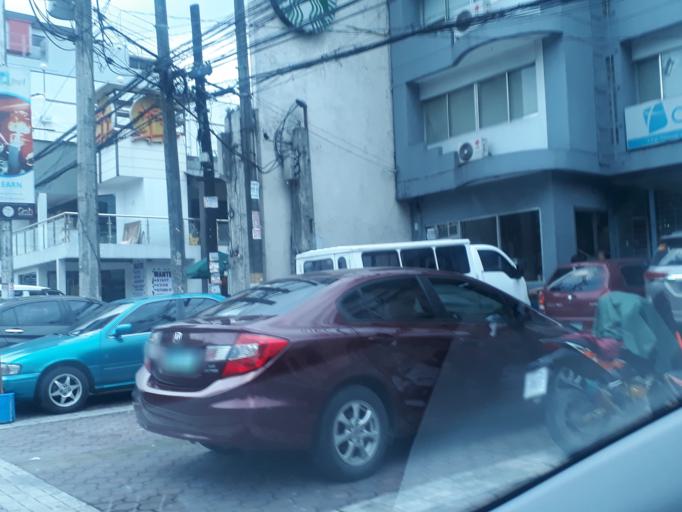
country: PH
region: Metro Manila
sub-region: Quezon City
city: Quezon City
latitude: 14.6331
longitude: 121.0430
